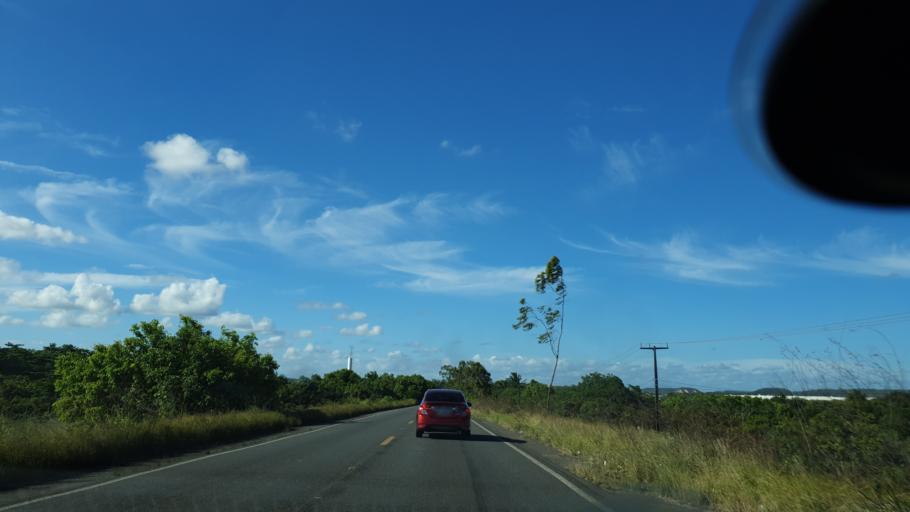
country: BR
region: Bahia
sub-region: Camacari
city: Camacari
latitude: -12.6503
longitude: -38.3036
